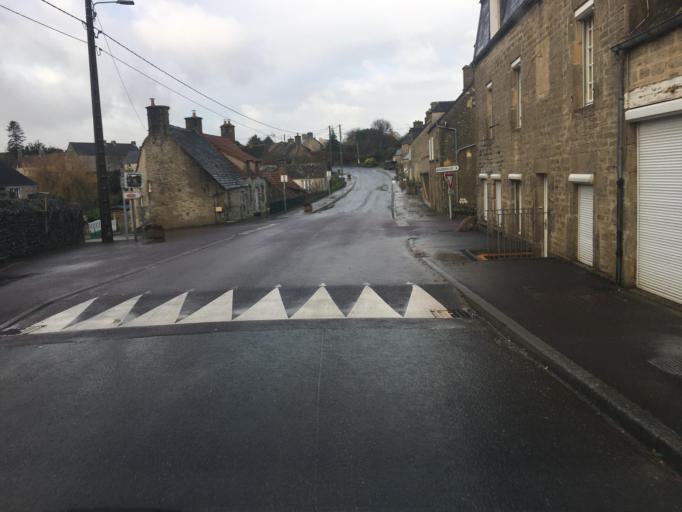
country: FR
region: Lower Normandy
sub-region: Departement de la Manche
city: Saint-Pierre-Eglise
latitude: 49.6707
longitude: -1.3363
